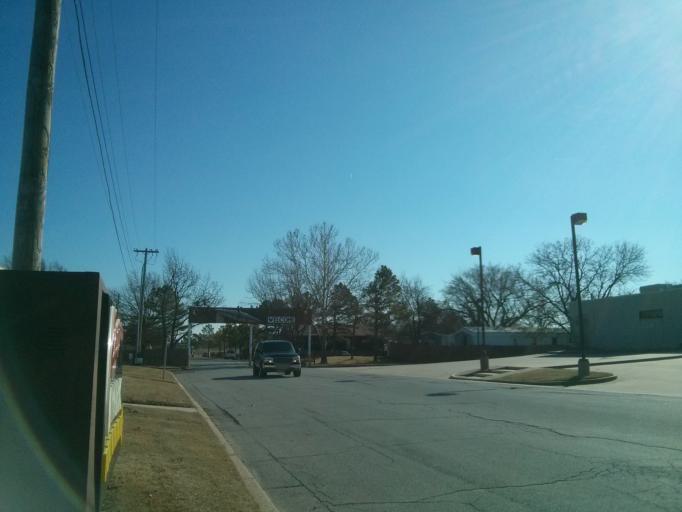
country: US
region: Oklahoma
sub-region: Tulsa County
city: Owasso
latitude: 36.1670
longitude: -95.8686
